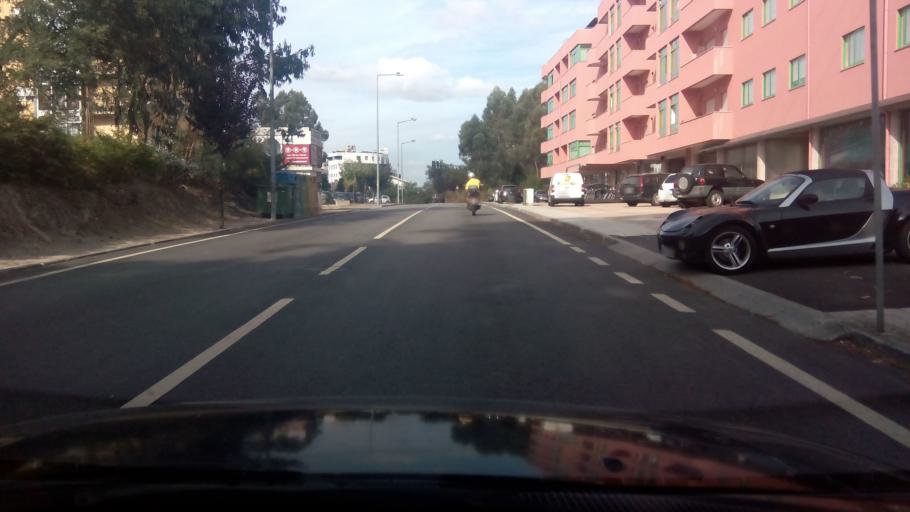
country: PT
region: Porto
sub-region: Paredes
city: Casteloes de Cepeda
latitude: 41.2029
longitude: -8.3436
